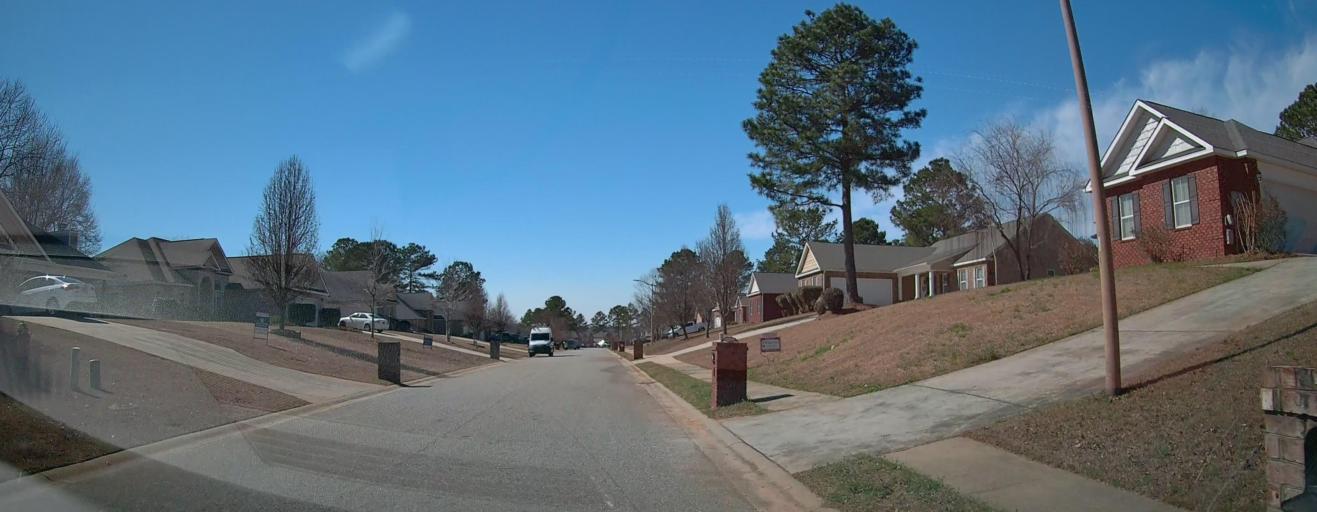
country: US
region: Georgia
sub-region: Houston County
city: Perry
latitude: 32.4985
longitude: -83.6530
